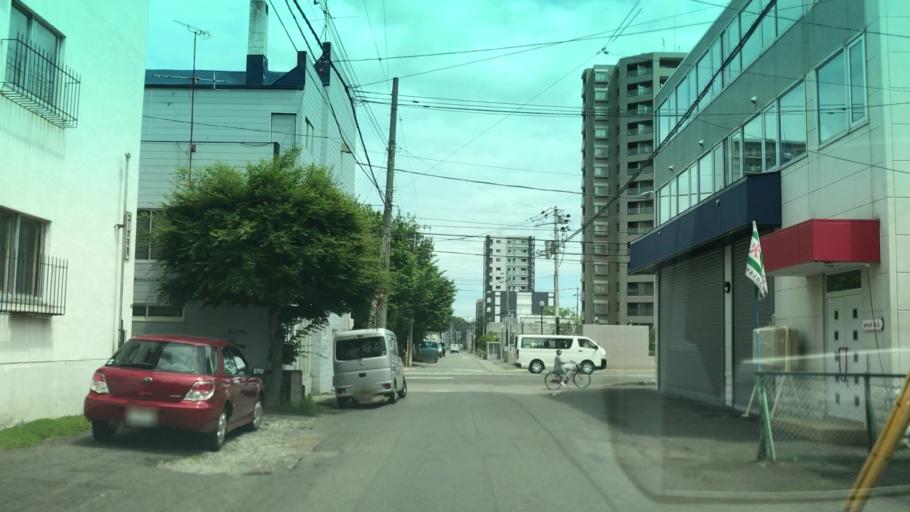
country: JP
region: Hokkaido
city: Sapporo
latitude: 43.0401
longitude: 141.3432
